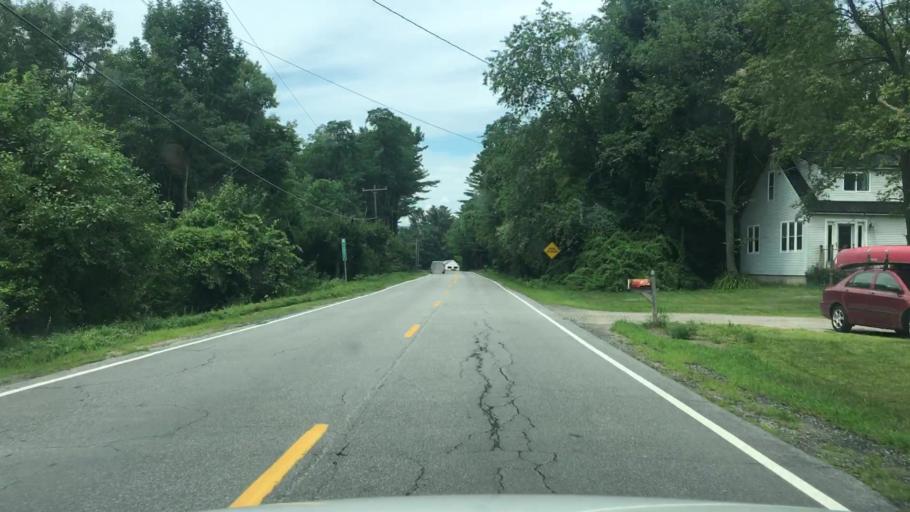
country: US
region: New Hampshire
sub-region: Grafton County
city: Rumney
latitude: 43.7816
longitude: -71.7620
